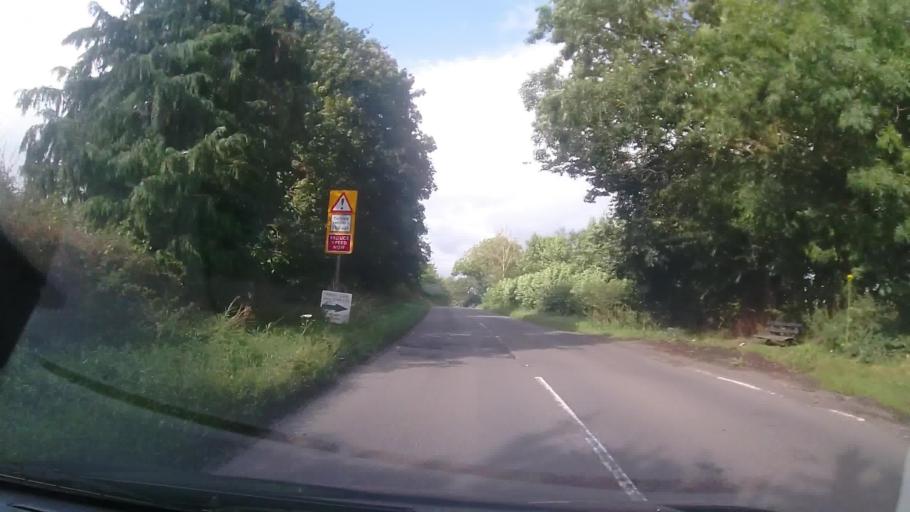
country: GB
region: England
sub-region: Shropshire
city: Bishop's Castle
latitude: 52.4920
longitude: -2.9906
